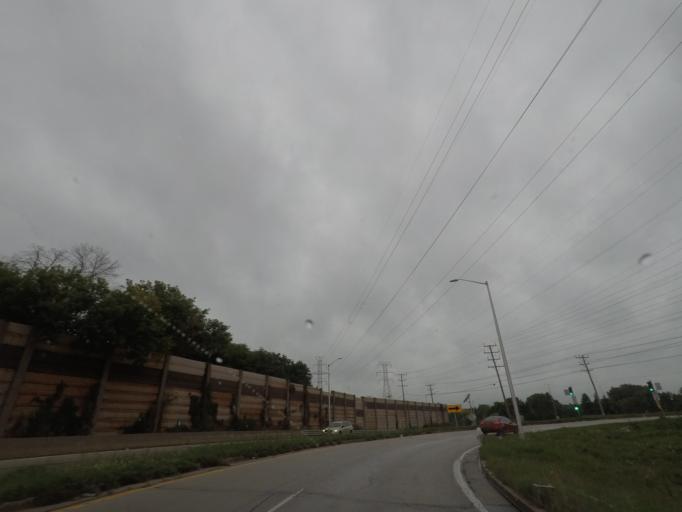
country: US
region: Wisconsin
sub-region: Milwaukee County
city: West Allis
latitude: 42.9982
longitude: -88.0366
